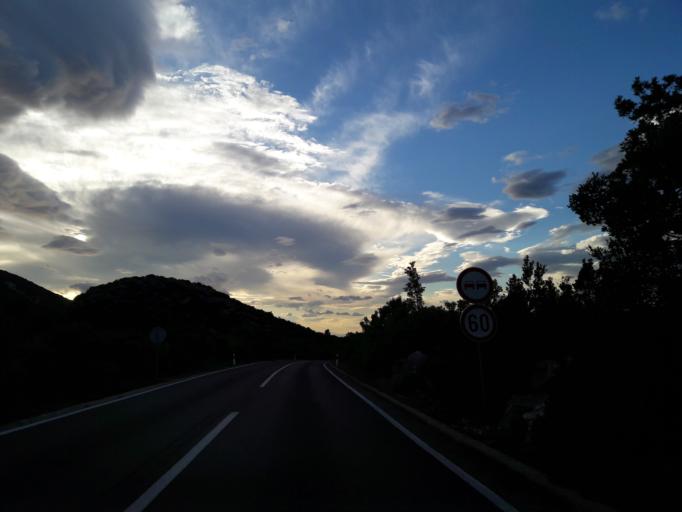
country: BA
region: Federation of Bosnia and Herzegovina
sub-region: Hercegovacko-Bosanski Kanton
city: Neum
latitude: 42.8928
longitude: 17.4965
